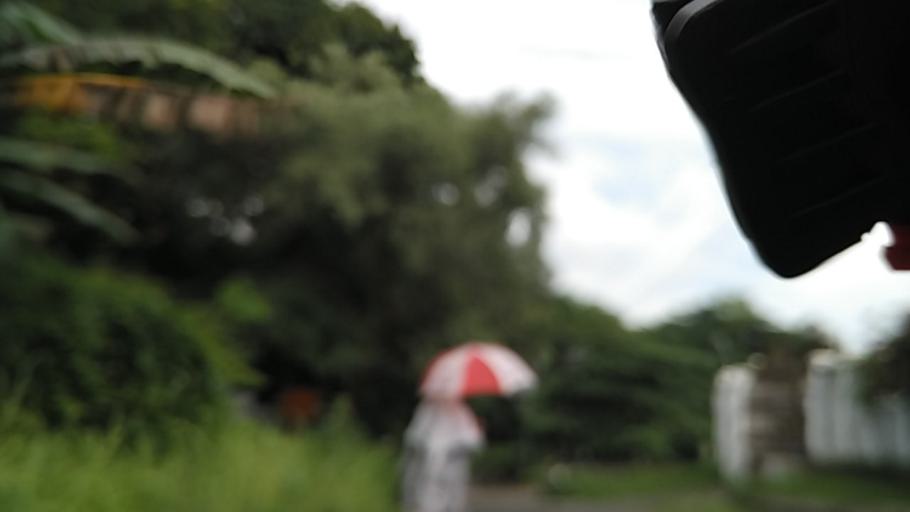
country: ID
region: Central Java
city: Semarang
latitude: -7.0056
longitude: 110.4165
